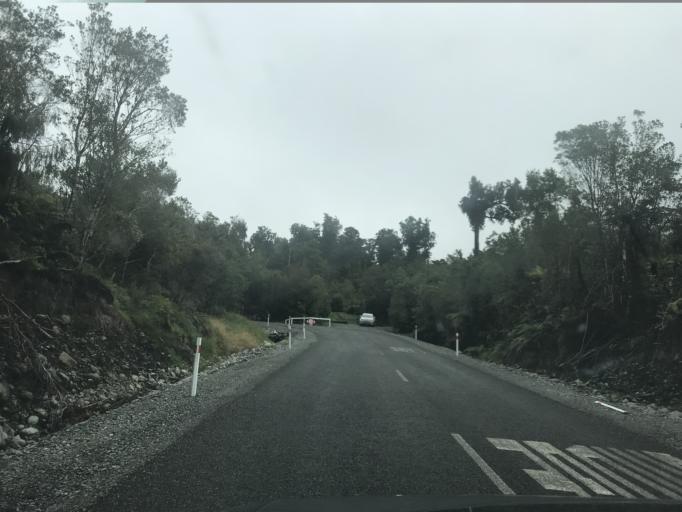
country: NZ
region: West Coast
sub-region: Westland District
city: Hokitika
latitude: -42.9557
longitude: 171.0208
